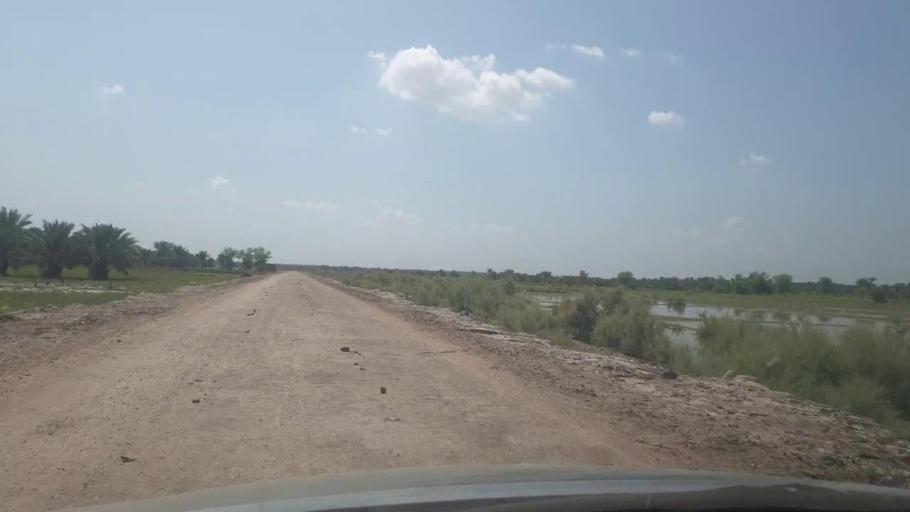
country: PK
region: Sindh
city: Khairpur
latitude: 27.5241
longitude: 68.8150
